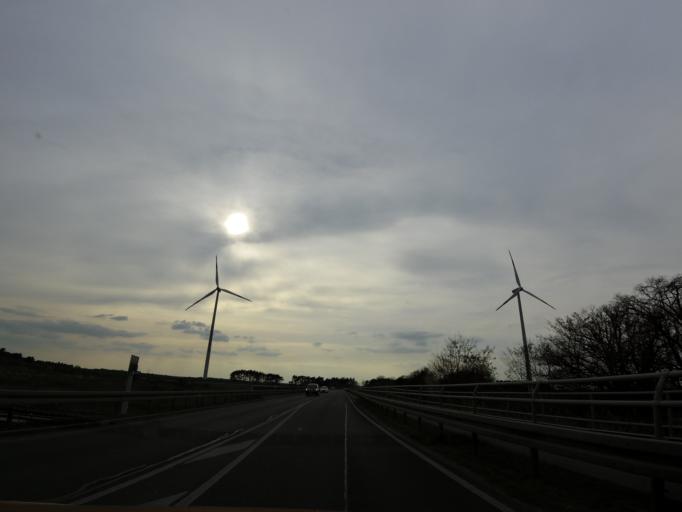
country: DE
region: Brandenburg
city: Mittenwalde
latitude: 52.2464
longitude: 13.5902
